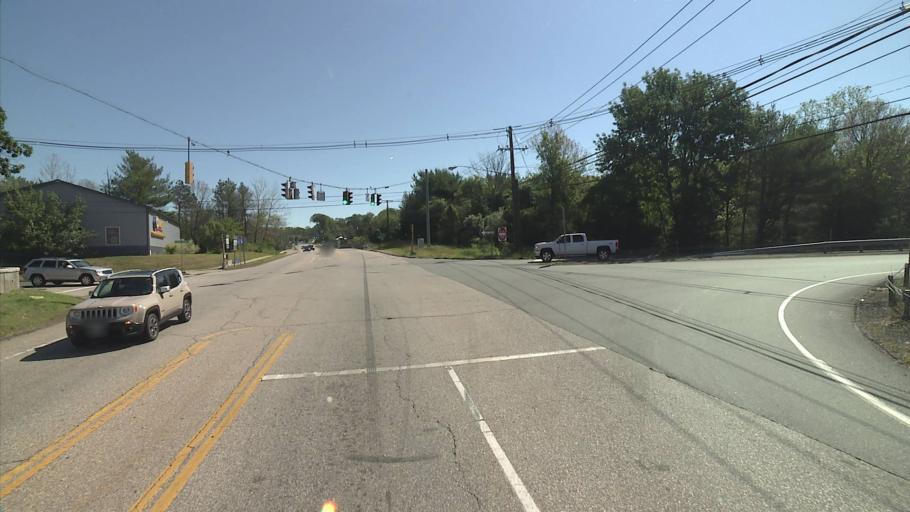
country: US
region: Connecticut
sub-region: New London County
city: Colchester
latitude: 41.5695
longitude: -72.3396
